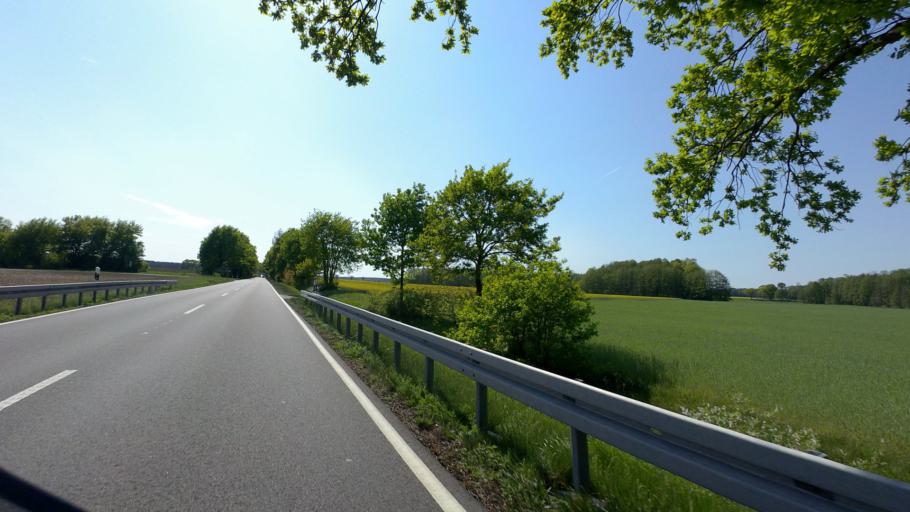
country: DE
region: Brandenburg
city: Neu Zauche
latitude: 52.0235
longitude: 14.0814
